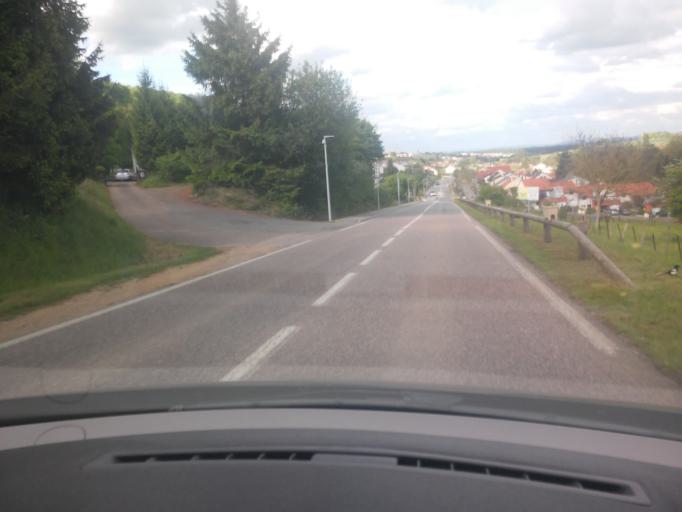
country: FR
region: Lorraine
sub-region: Departement de la Moselle
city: Marange-Silvange
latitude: 49.1918
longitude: 6.0807
